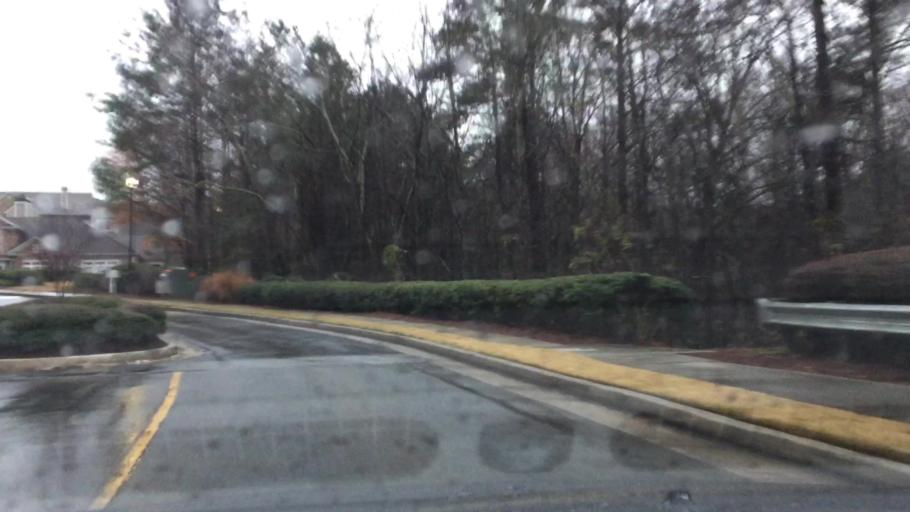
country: US
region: Georgia
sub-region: Cobb County
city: Marietta
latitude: 34.0110
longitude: -84.5546
